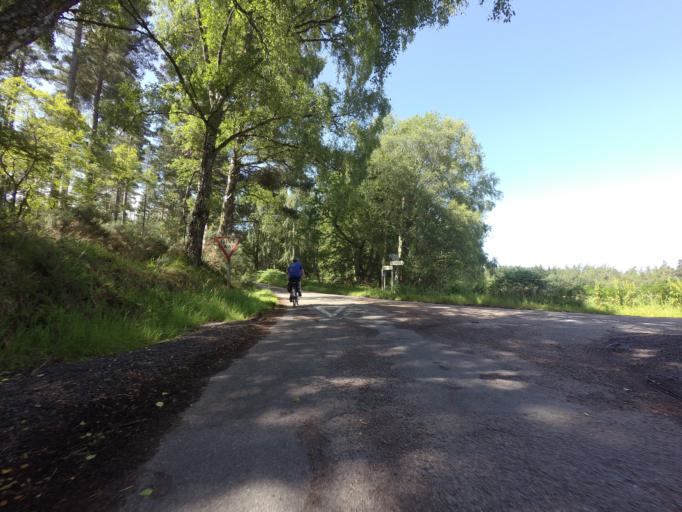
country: GB
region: Scotland
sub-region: Highland
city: Nairn
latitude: 57.5074
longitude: -3.9045
